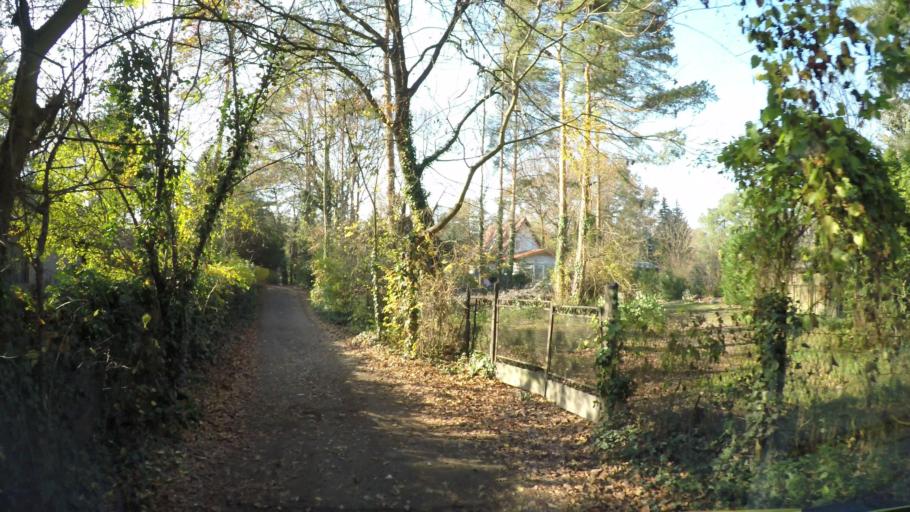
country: HU
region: Pest
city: God
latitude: 47.6676
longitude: 19.1077
